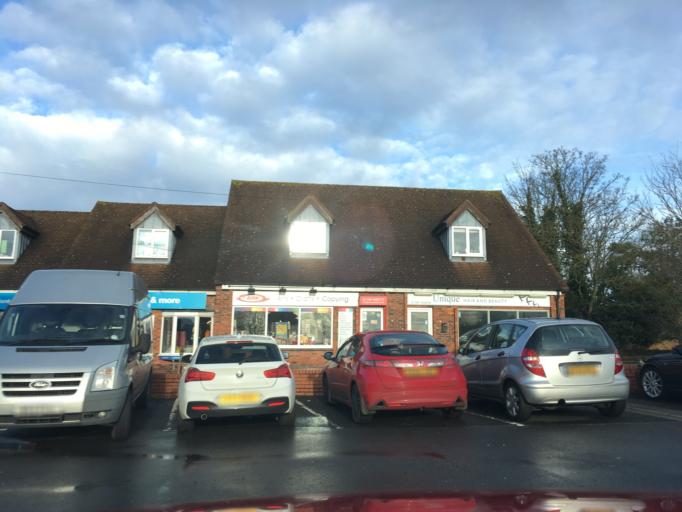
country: GB
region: England
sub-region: Warwickshire
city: Alcester
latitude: 52.2153
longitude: -1.8712
